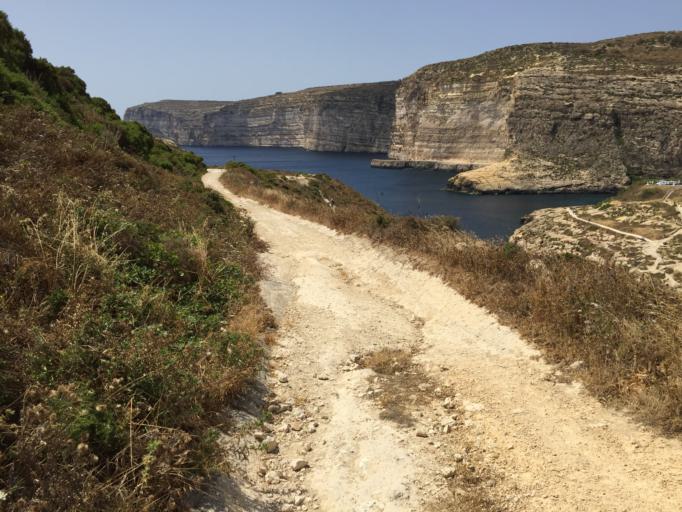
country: MT
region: Saint Lucia
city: Saint Lucia
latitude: 36.0265
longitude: 14.2166
